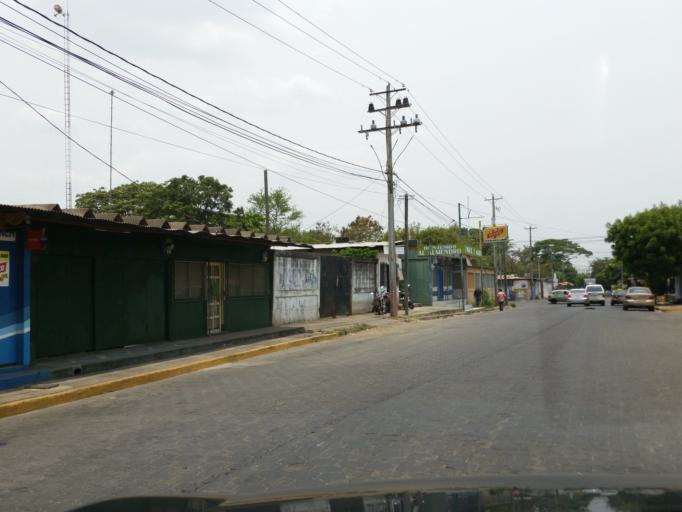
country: NI
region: Managua
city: Managua
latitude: 12.1494
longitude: -86.2230
